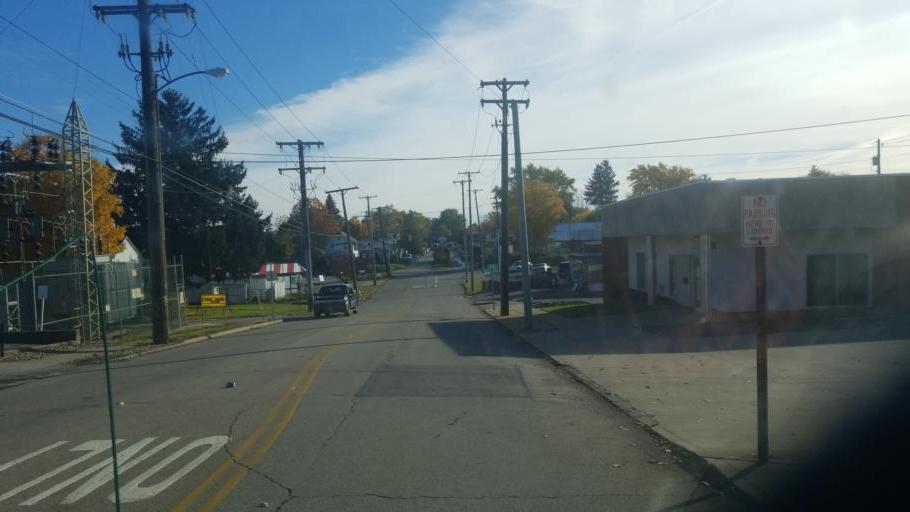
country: US
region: Ohio
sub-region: Richland County
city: Mansfield
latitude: 40.7476
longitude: -82.5228
